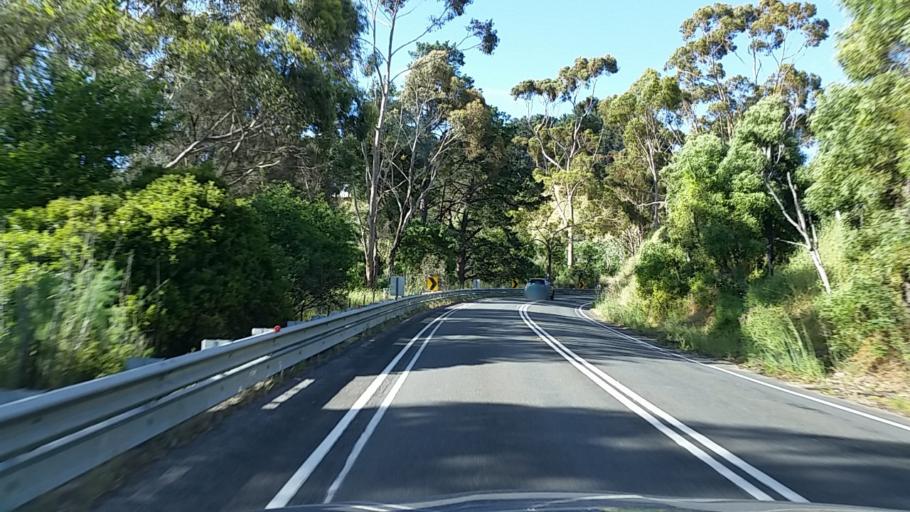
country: AU
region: South Australia
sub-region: Mount Barker
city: Meadows
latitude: -35.2371
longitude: 138.7656
